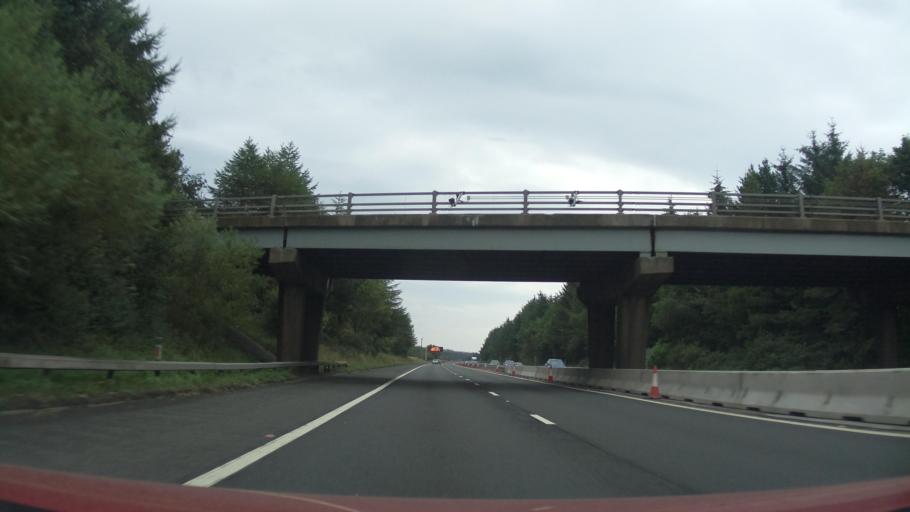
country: GB
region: Scotland
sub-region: North Lanarkshire
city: Harthill
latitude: 55.8655
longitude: -3.7508
